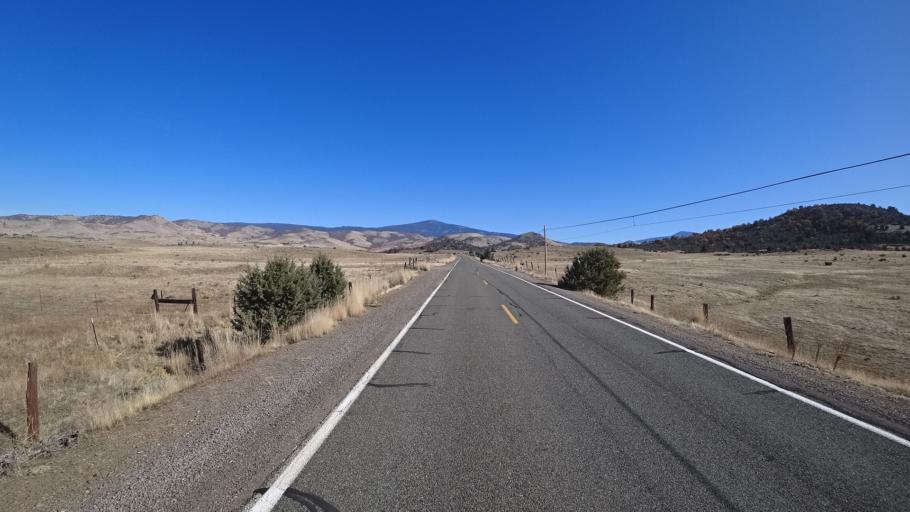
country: US
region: California
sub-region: Siskiyou County
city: Montague
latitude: 41.8044
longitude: -122.3989
